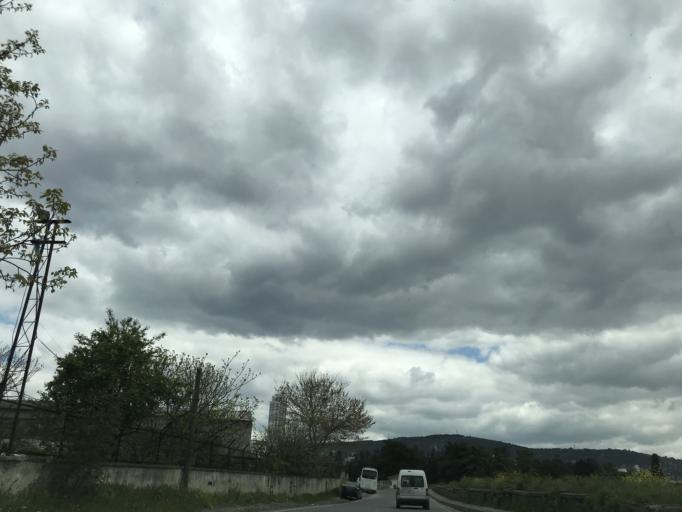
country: TR
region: Istanbul
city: Maltepe
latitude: 40.9034
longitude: 29.2105
